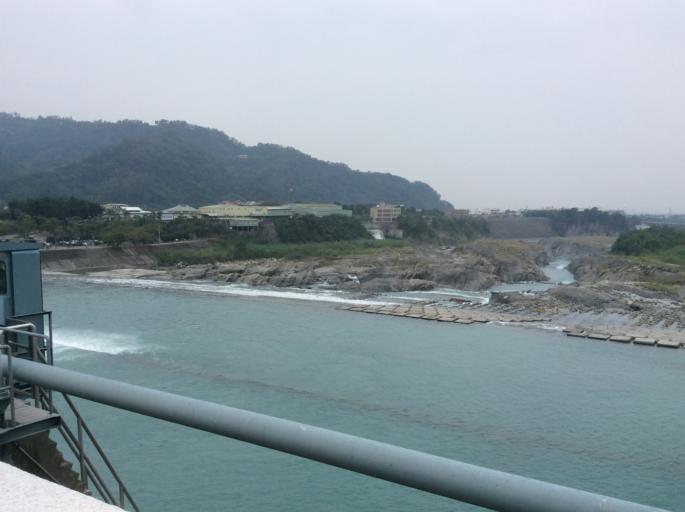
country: TW
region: Taiwan
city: Fengyuan
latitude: 24.2826
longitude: 120.7691
